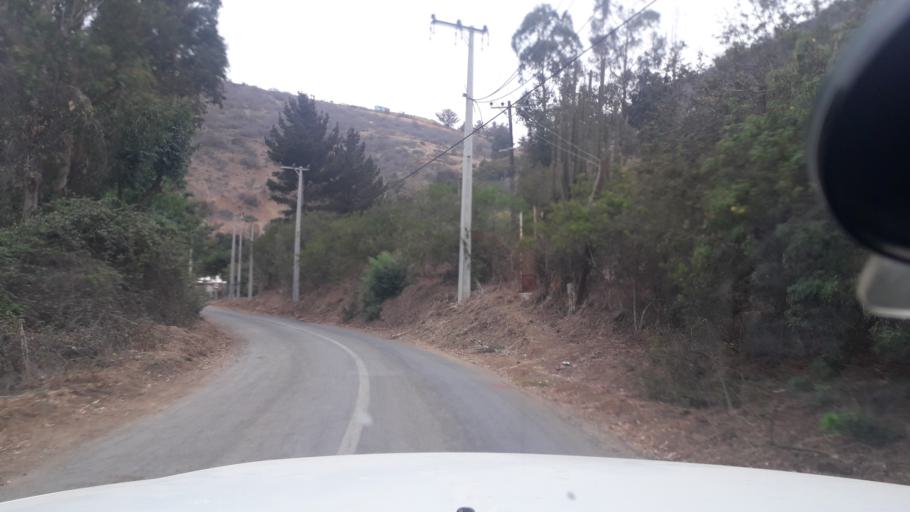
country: CL
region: Valparaiso
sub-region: Provincia de Valparaiso
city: Valparaiso
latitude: -33.1125
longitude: -71.6571
